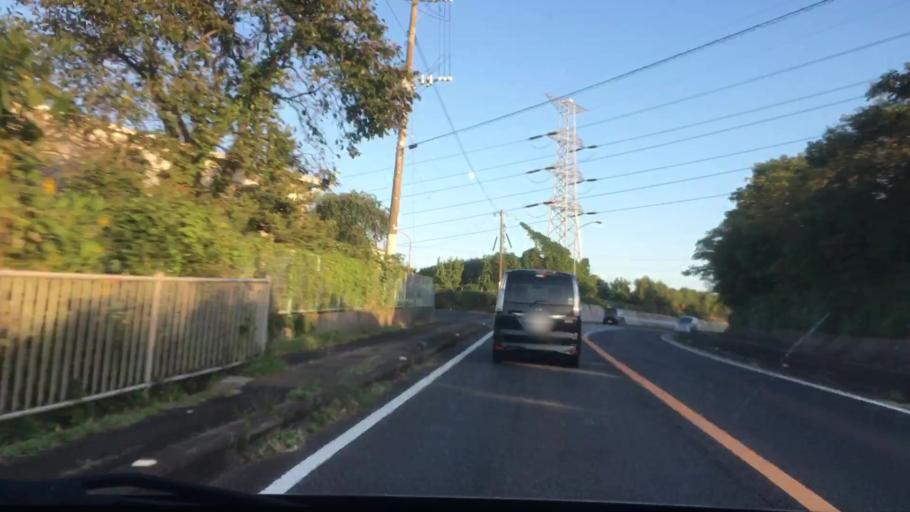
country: JP
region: Nagasaki
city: Sasebo
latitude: 33.0762
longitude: 129.7586
